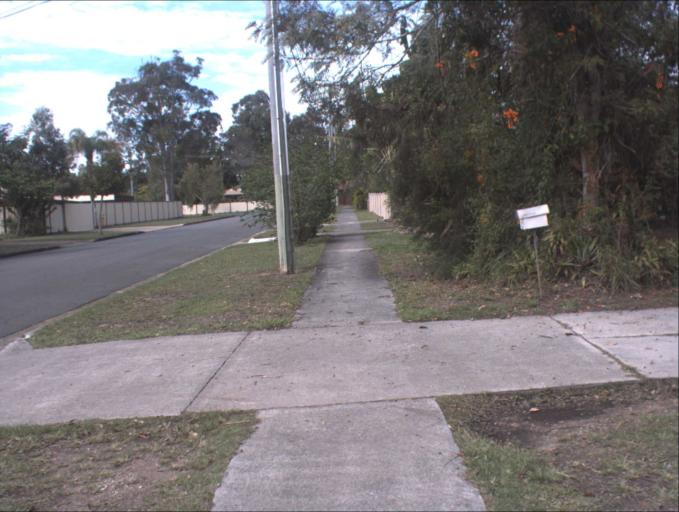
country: AU
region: Queensland
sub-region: Logan
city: Waterford West
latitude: -27.6798
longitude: 153.1102
